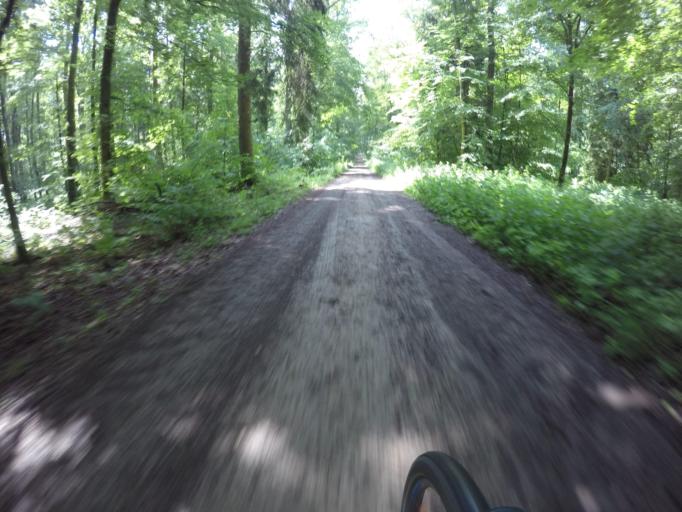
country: DE
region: Baden-Wuerttemberg
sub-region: Regierungsbezirk Stuttgart
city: Nufringen
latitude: 48.6400
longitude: 8.8599
